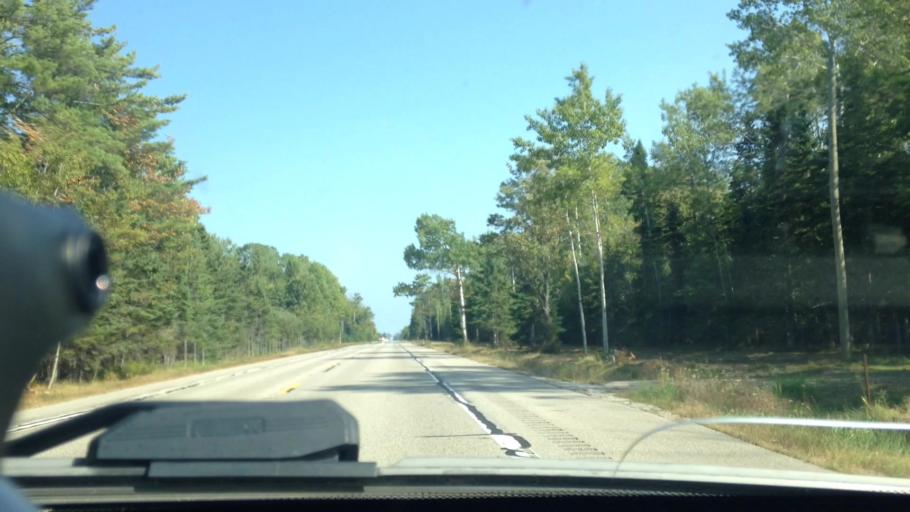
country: US
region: Michigan
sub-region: Luce County
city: Newberry
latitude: 46.3034
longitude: -85.3589
